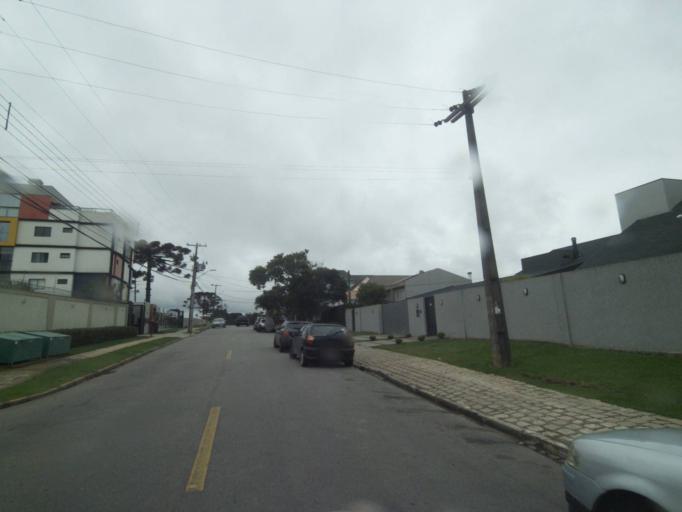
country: BR
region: Parana
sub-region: Curitiba
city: Curitiba
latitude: -25.4217
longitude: -49.3322
